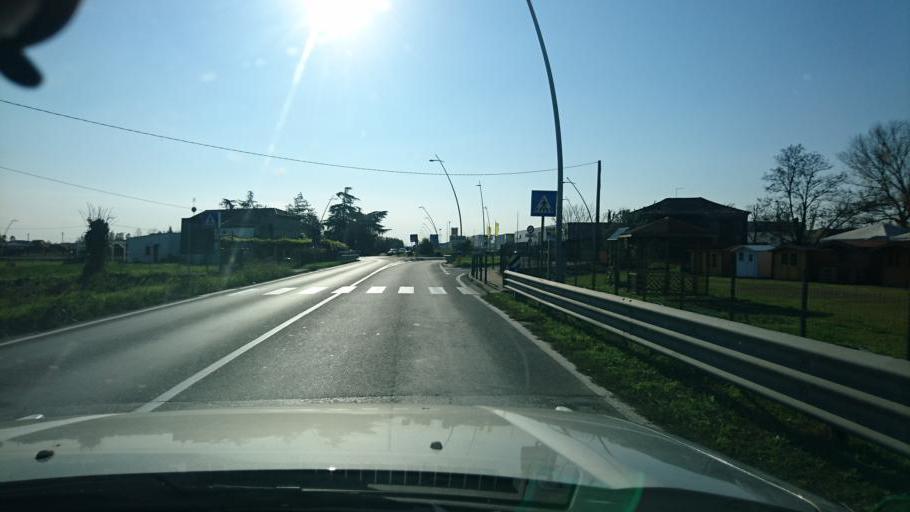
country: IT
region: Veneto
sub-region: Provincia di Padova
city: Monselice
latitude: 45.2183
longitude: 11.7552
